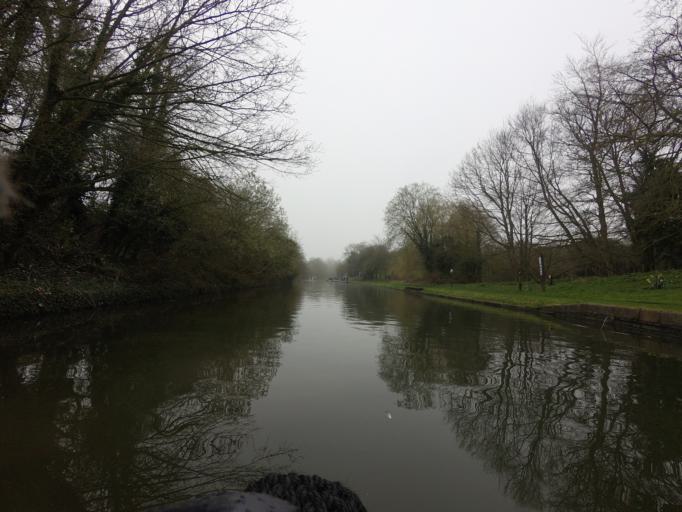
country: GB
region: England
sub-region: Hertfordshire
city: Tring
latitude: 51.8136
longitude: -0.6476
